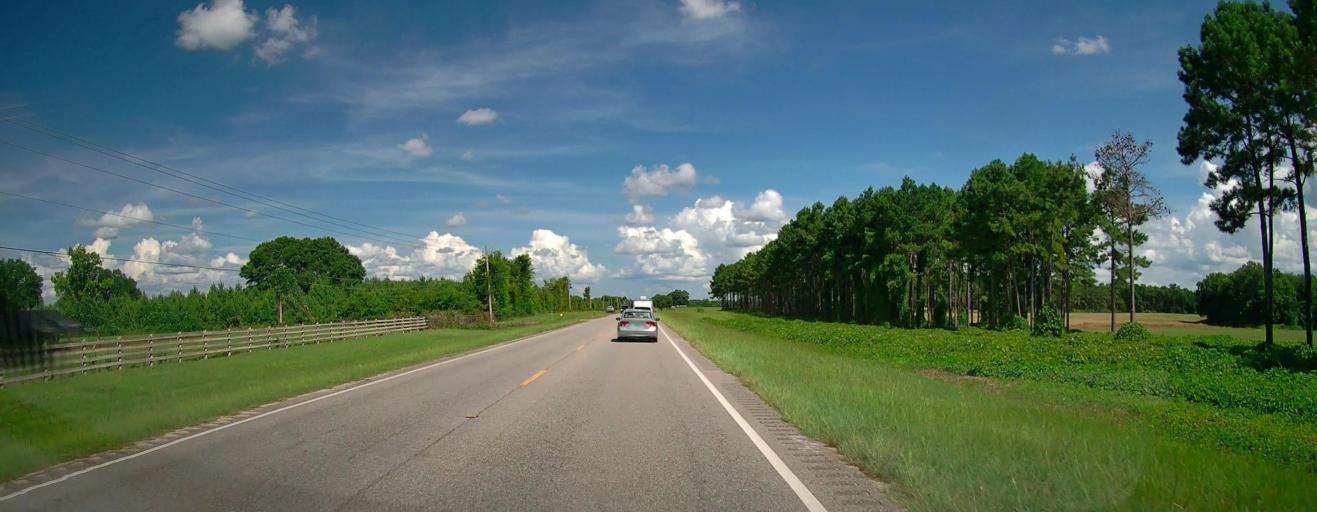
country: US
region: Alabama
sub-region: Elmore County
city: Tallassee
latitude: 32.3906
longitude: -85.8955
